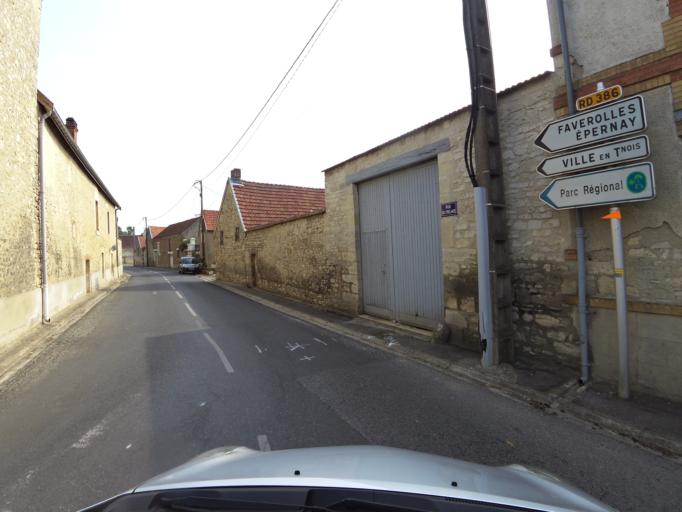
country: FR
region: Champagne-Ardenne
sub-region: Departement de la Marne
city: Jonchery-sur-Vesle
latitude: 49.2440
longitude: 3.7822
